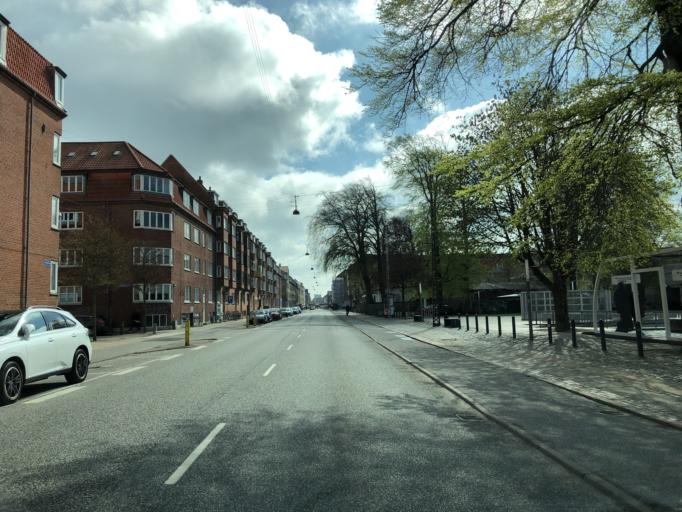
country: DK
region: North Denmark
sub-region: Alborg Kommune
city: Aalborg
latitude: 57.0546
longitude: 9.8989
